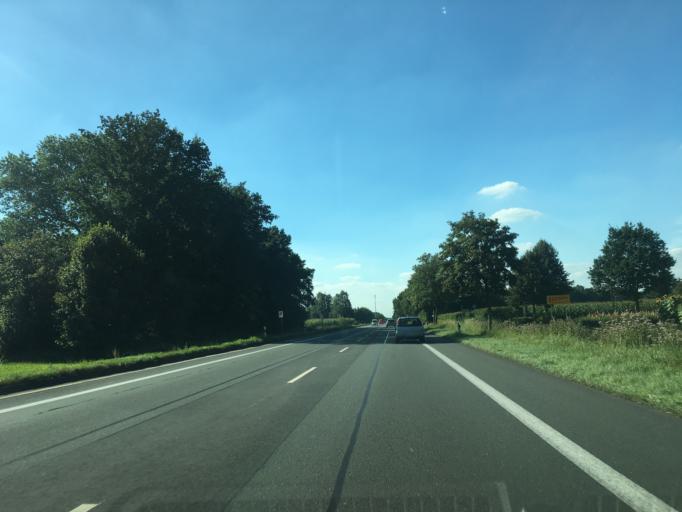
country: DE
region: North Rhine-Westphalia
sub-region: Regierungsbezirk Munster
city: Beelen
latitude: 51.9114
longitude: 8.1699
